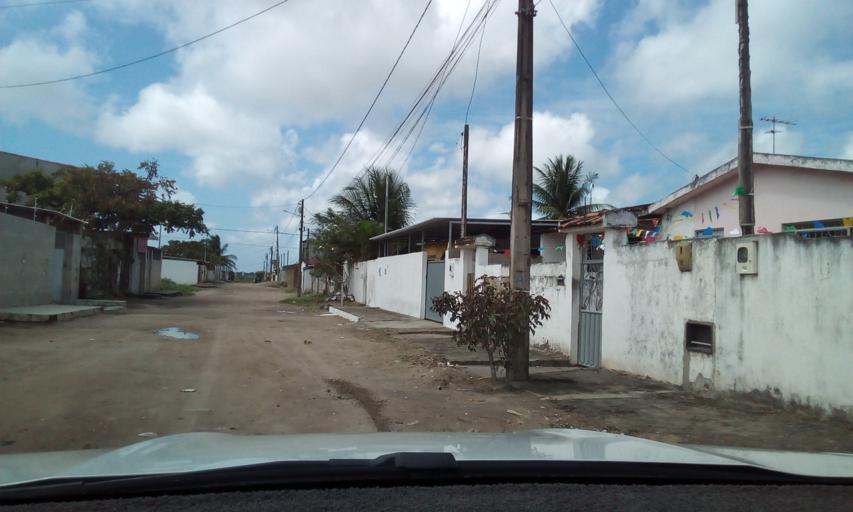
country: BR
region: Paraiba
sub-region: Santa Rita
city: Santa Rita
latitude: -7.1415
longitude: -34.9647
